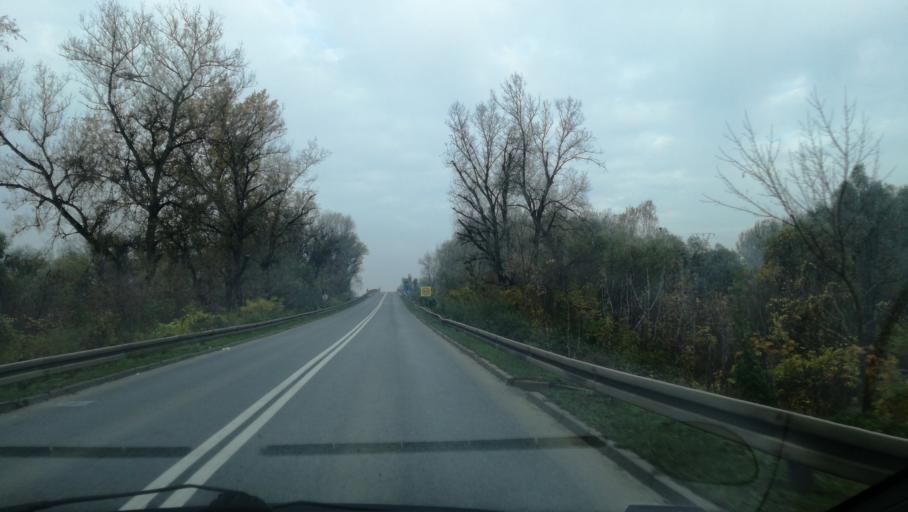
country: RS
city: Taras
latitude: 45.3957
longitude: 20.2166
